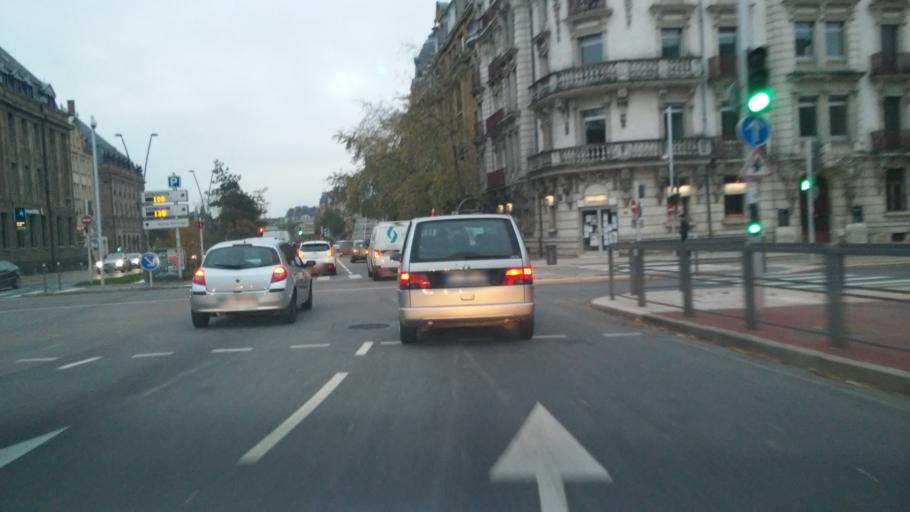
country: FR
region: Lorraine
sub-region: Departement de la Moselle
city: Metz
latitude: 49.1117
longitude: 6.1707
